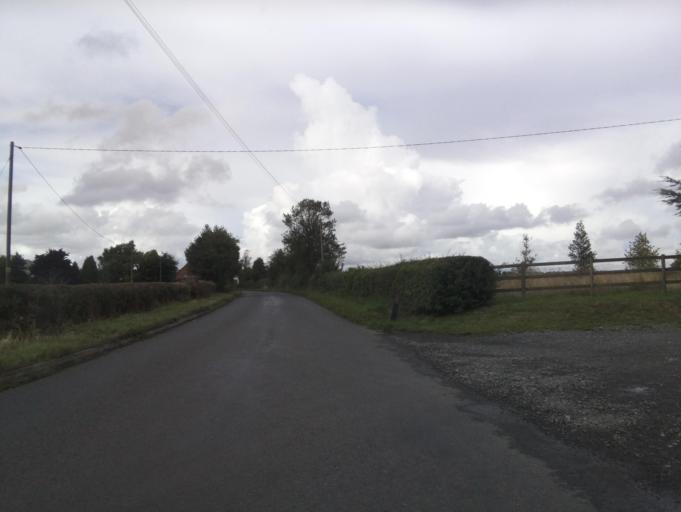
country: GB
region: England
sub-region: Worcestershire
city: Kidderminster
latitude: 52.3429
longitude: -2.1951
